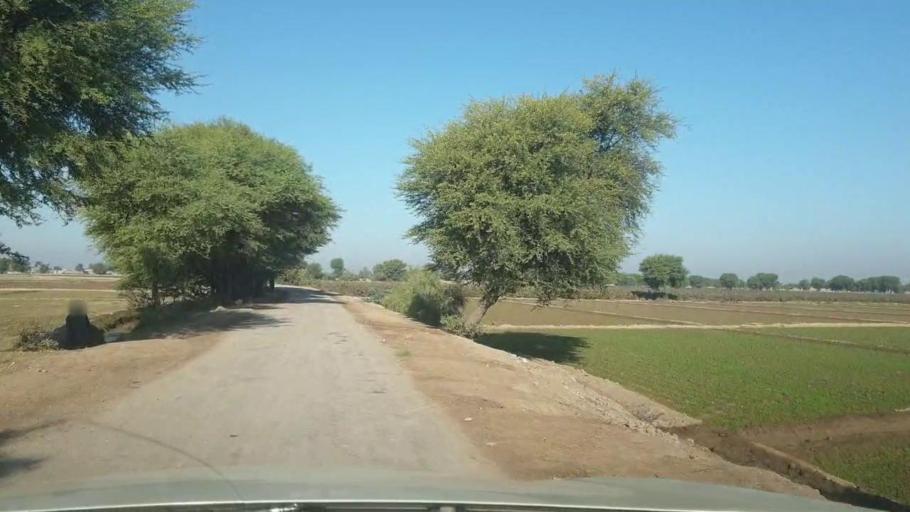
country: PK
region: Sindh
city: Bhan
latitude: 26.5494
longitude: 67.6665
